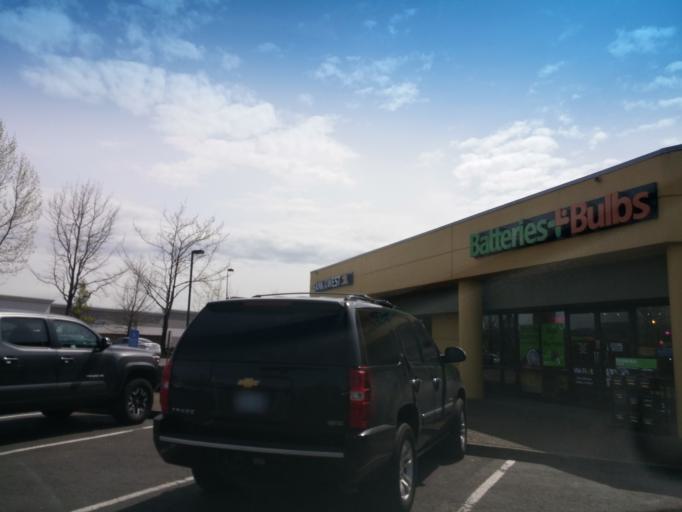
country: US
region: Oregon
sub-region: Washington County
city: Rockcreek
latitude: 45.5379
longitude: -122.8669
